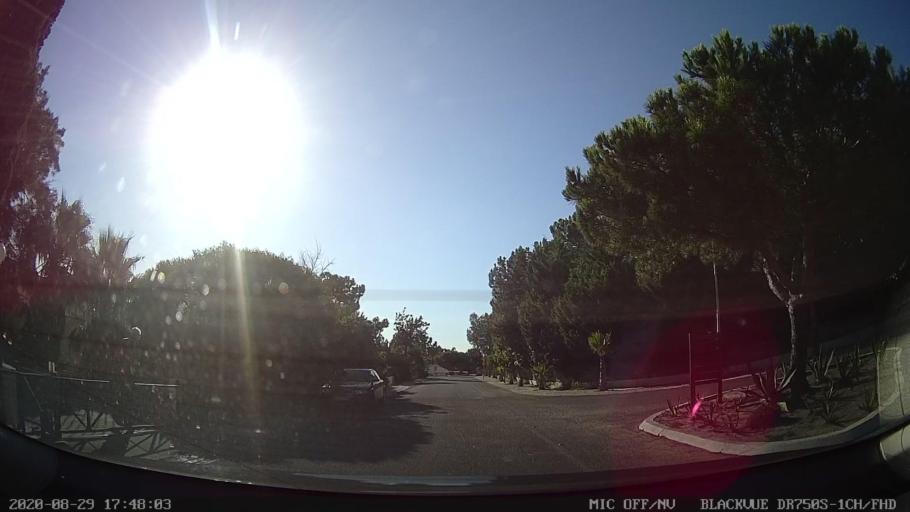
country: PT
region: Setubal
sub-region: Setubal
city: Setubal
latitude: 38.4573
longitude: -8.8600
